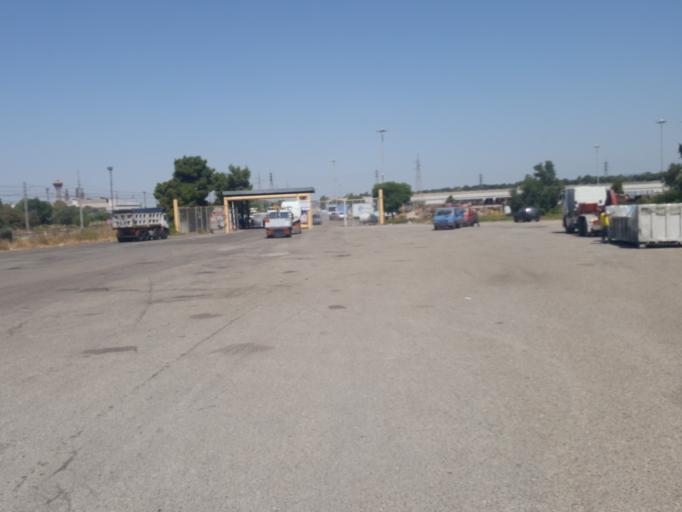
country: IT
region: Apulia
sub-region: Provincia di Taranto
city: Statte
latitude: 40.5066
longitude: 17.1914
